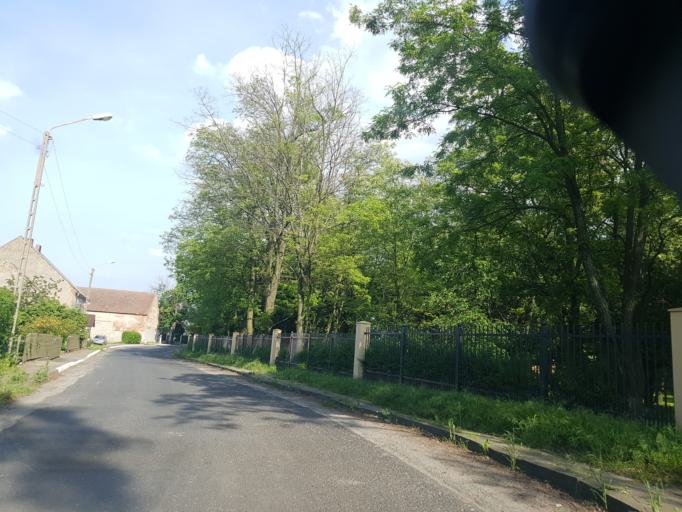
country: PL
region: Lower Silesian Voivodeship
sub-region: Powiat strzelinski
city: Wiazow
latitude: 50.8554
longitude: 17.1838
